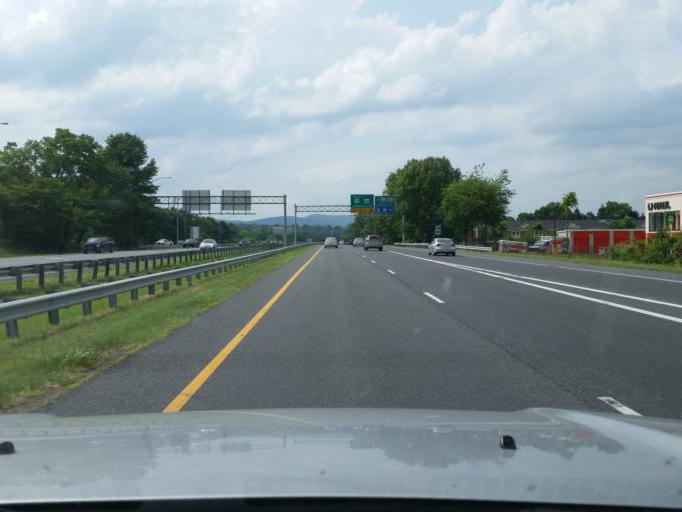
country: US
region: Maryland
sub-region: Frederick County
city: Frederick
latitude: 39.4011
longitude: -77.4276
